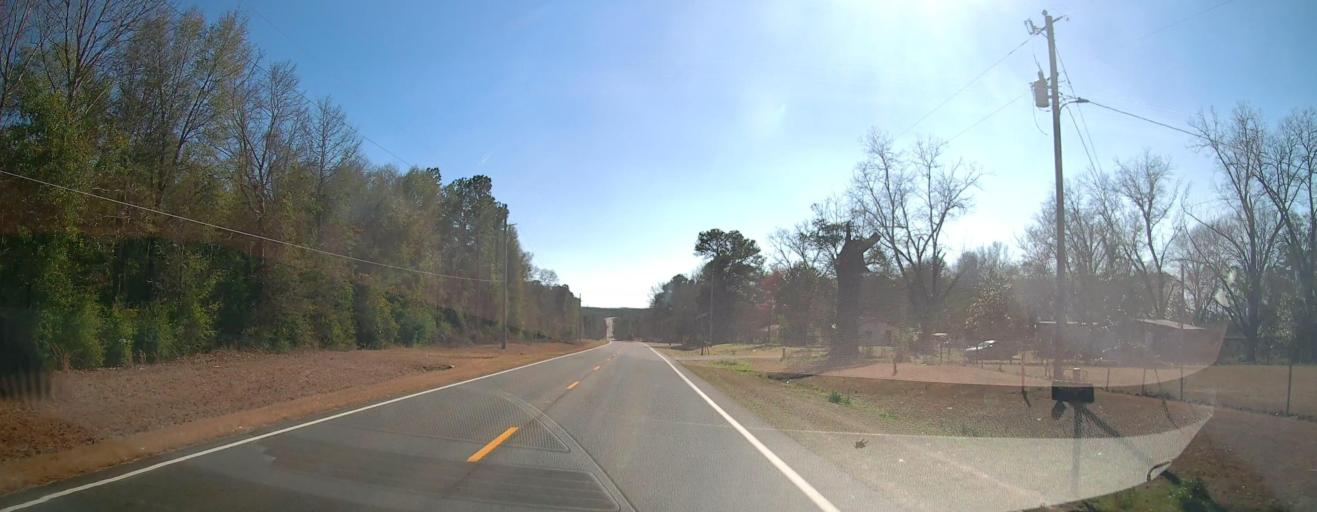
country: US
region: Georgia
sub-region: Macon County
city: Oglethorpe
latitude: 32.2339
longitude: -84.0963
